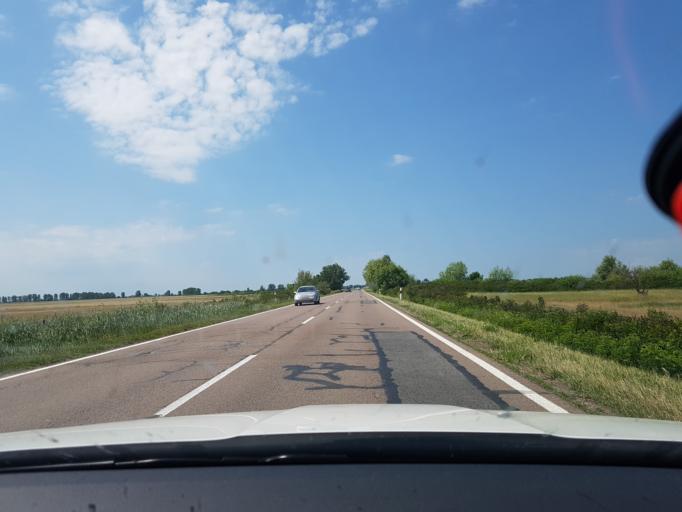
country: HU
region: Hajdu-Bihar
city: Hortobagy
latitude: 47.5895
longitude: 21.0445
